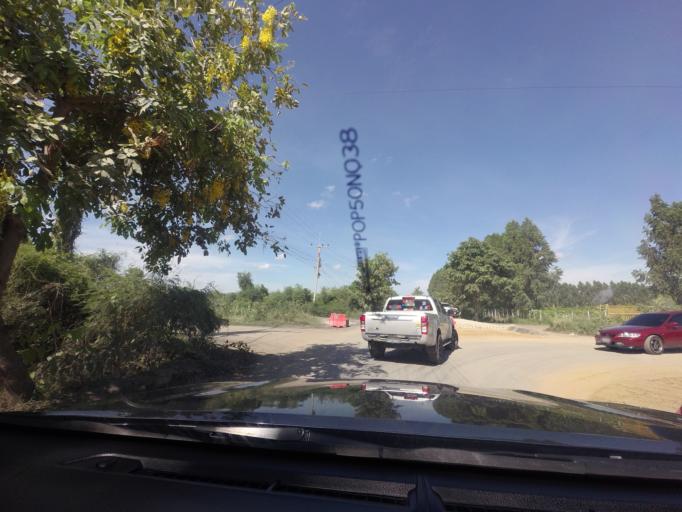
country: TH
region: Suphan Buri
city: Song Phi Nong
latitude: 14.1631
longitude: 100.0034
